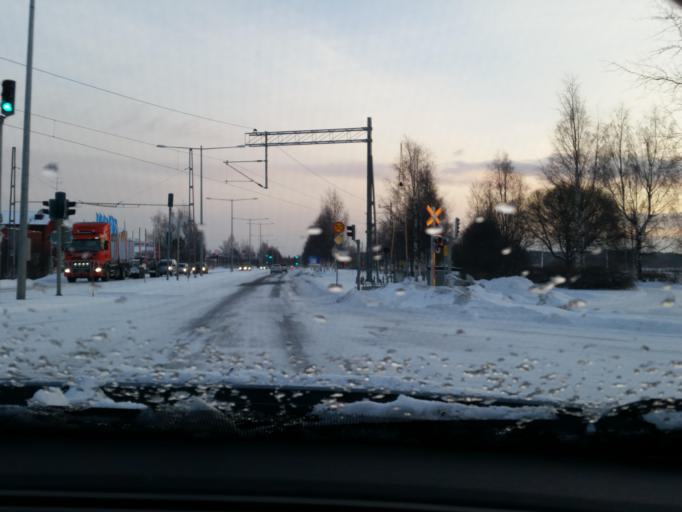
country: SE
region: Norrbotten
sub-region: Pitea Kommun
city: Pitea
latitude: 65.3168
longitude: 21.4710
